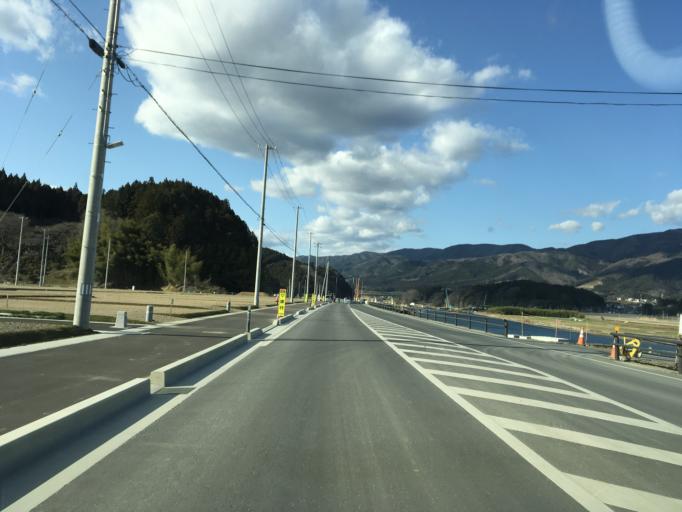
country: JP
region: Iwate
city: Ofunato
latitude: 39.0102
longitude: 141.6162
